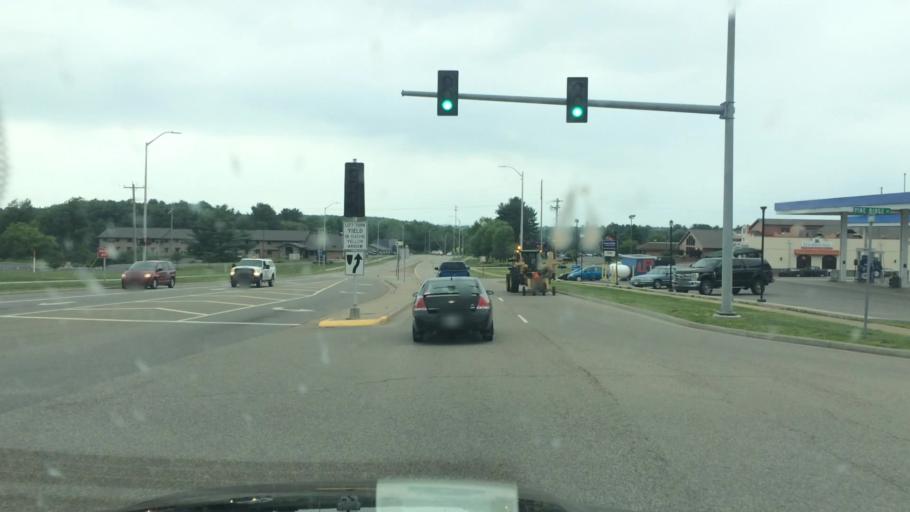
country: US
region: Wisconsin
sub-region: Lincoln County
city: Merrill
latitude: 45.1780
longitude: -89.6520
